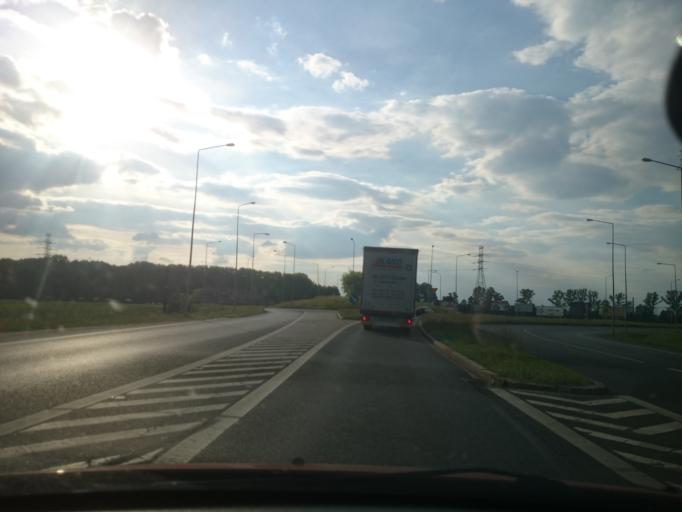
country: PL
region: Opole Voivodeship
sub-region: Powiat opolski
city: Opole
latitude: 50.6405
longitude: 17.9966
